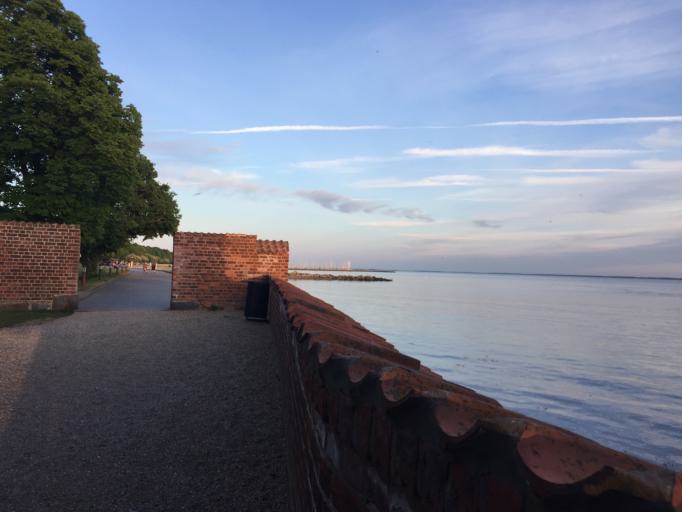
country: DK
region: South Denmark
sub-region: Sonderborg Kommune
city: Sonderborg
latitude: 54.9063
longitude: 9.7833
